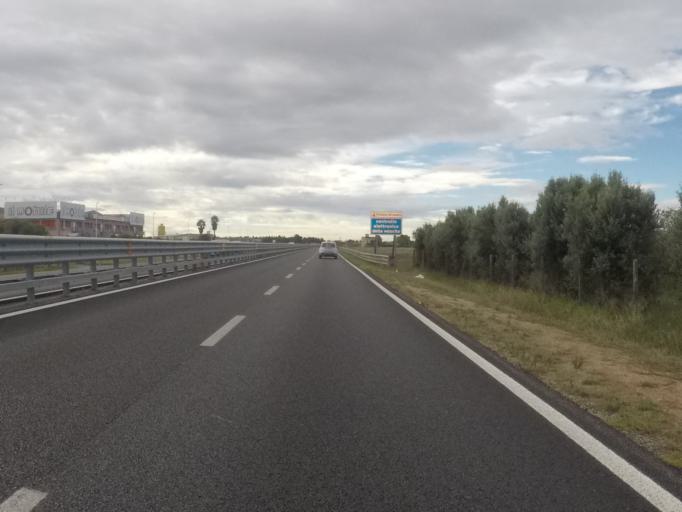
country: IT
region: Sardinia
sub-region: Provincia di Cagliari
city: Decimomannu
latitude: 39.3131
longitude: 8.9810
